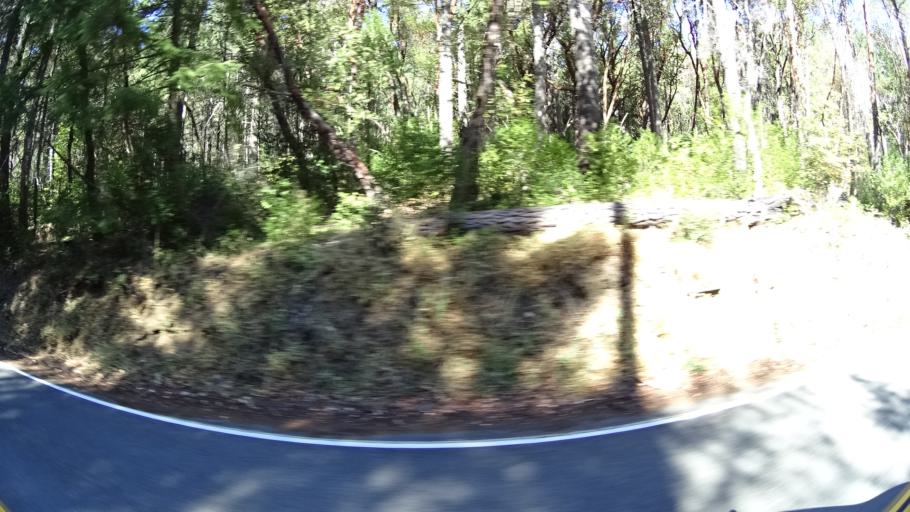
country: US
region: California
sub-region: Siskiyou County
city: Happy Camp
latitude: 41.3771
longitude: -123.4437
